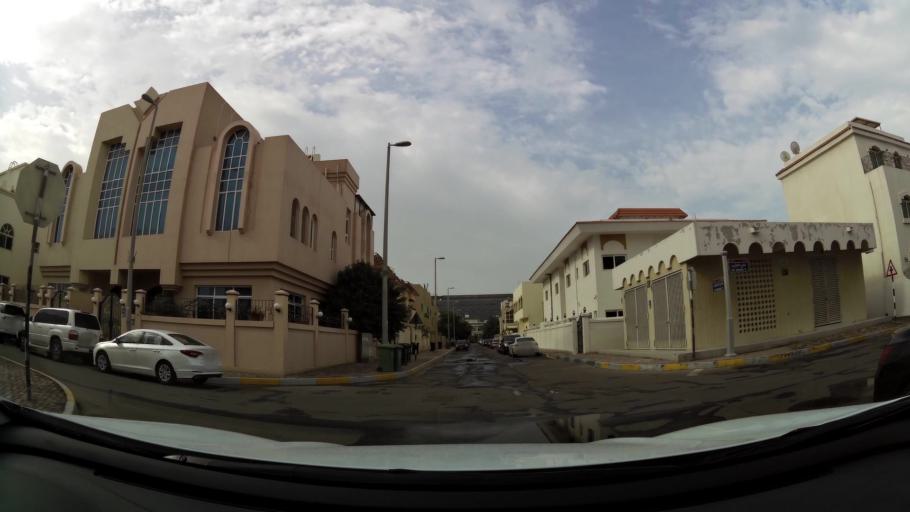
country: AE
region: Abu Dhabi
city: Abu Dhabi
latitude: 24.4517
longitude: 54.4002
